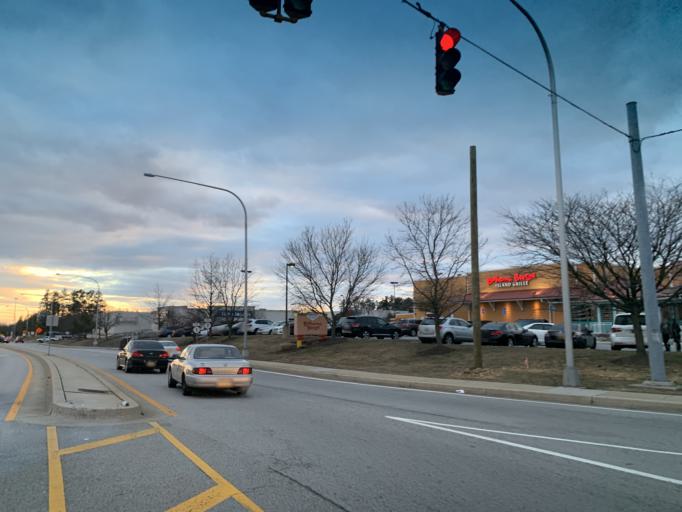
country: US
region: Delaware
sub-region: New Castle County
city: Bear
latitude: 39.6755
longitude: -75.6494
